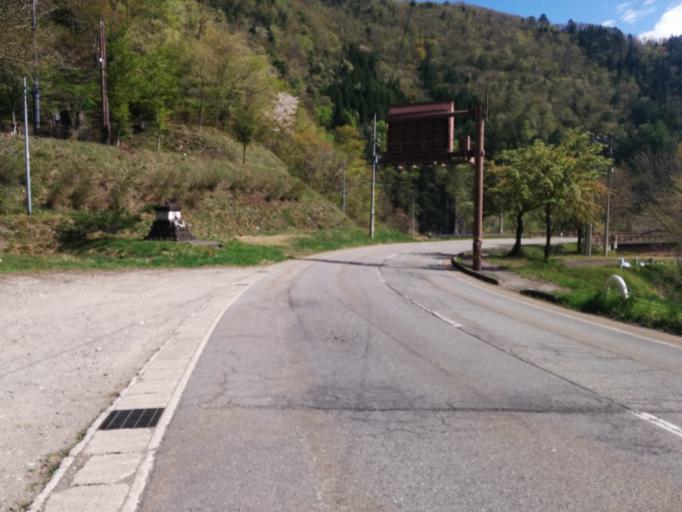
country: JP
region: Toyama
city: Fukumitsu
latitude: 36.2535
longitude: 136.8901
